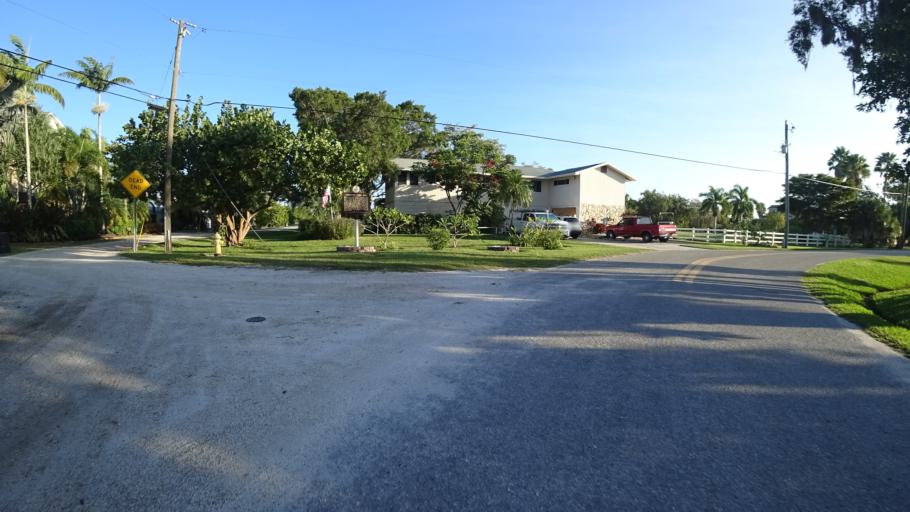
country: US
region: Florida
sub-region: Manatee County
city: Memphis
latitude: 27.5685
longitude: -82.5931
